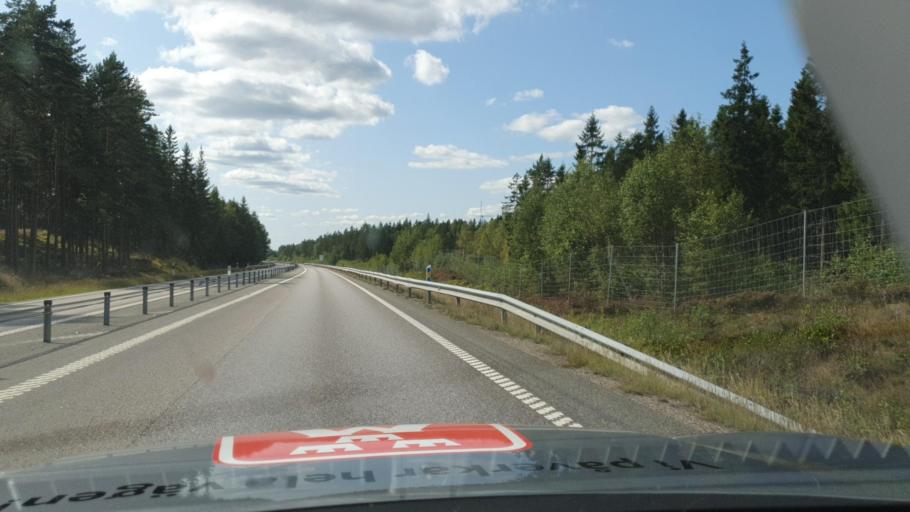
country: SE
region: Joenkoeping
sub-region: Varnamo Kommun
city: Rydaholm
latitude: 56.8938
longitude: 14.2962
